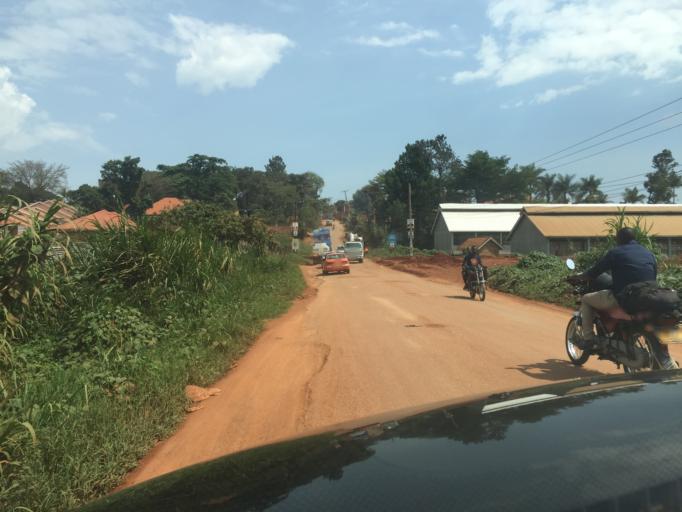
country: UG
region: Central Region
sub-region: Wakiso District
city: Kireka
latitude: 0.3943
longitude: 32.6241
